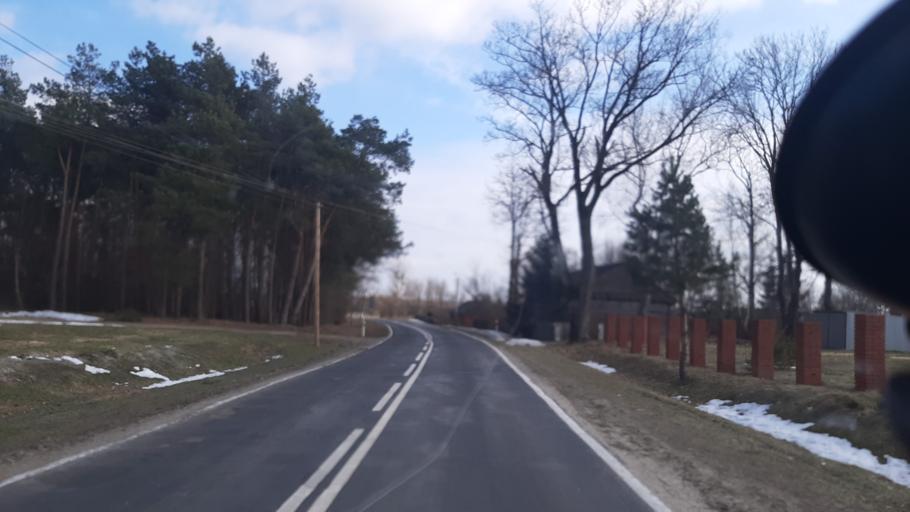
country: PL
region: Lublin Voivodeship
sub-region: Powiat wlodawski
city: Urszulin
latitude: 51.4945
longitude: 23.2203
